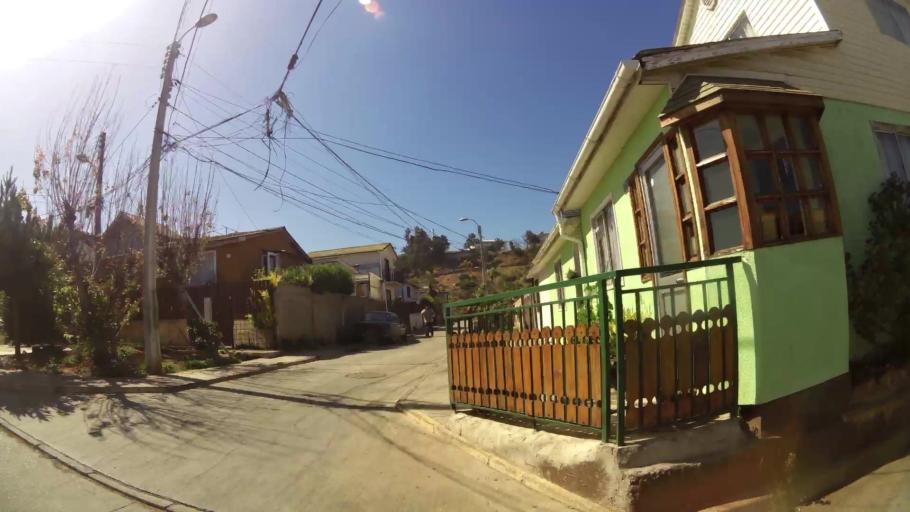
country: CL
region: Valparaiso
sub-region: Provincia de Valparaiso
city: Valparaiso
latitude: -33.0453
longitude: -71.6535
